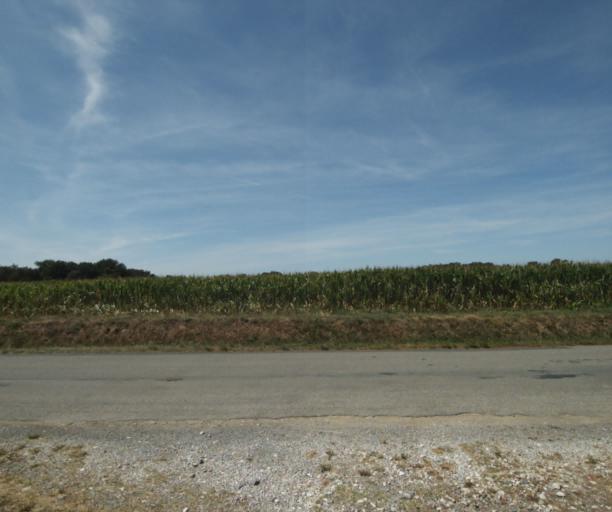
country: FR
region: Midi-Pyrenees
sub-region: Departement de la Haute-Garonne
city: Revel
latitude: 43.5037
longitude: 2.0279
